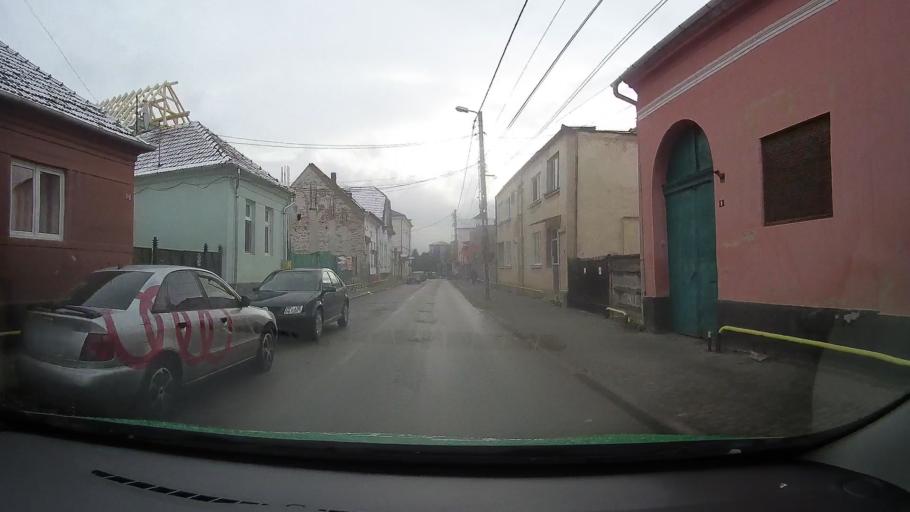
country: RO
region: Hunedoara
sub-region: Oras Hateg
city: Hateg
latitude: 45.6115
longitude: 22.9485
